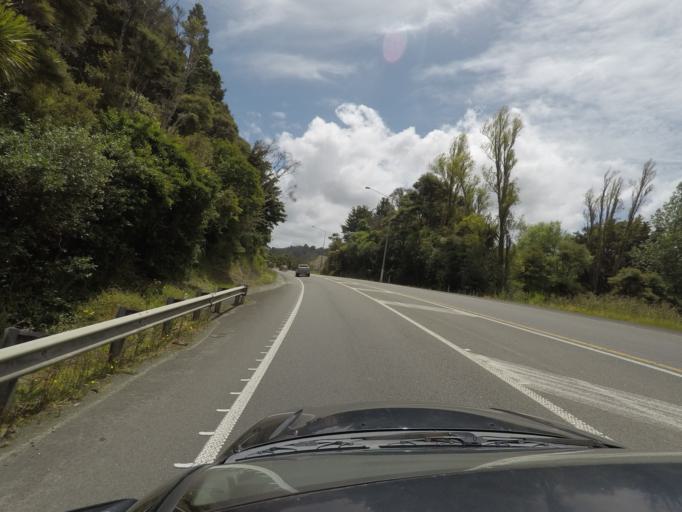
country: NZ
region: Auckland
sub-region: Auckland
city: Warkworth
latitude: -36.5207
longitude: 174.6749
